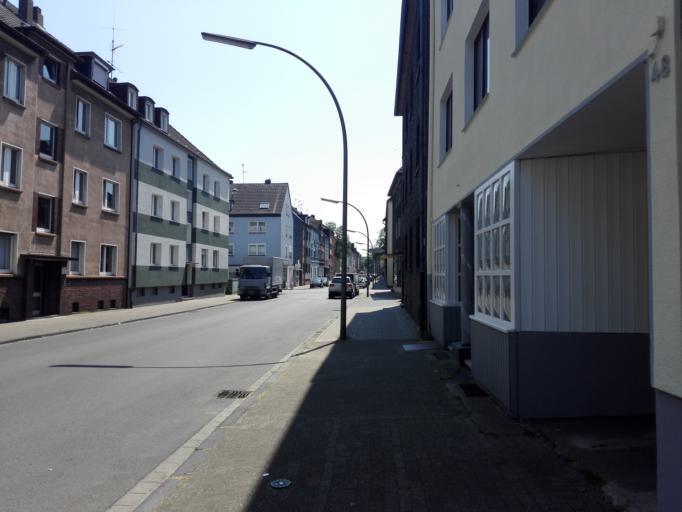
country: DE
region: North Rhine-Westphalia
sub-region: Regierungsbezirk Munster
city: Gladbeck
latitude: 51.5338
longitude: 7.0242
